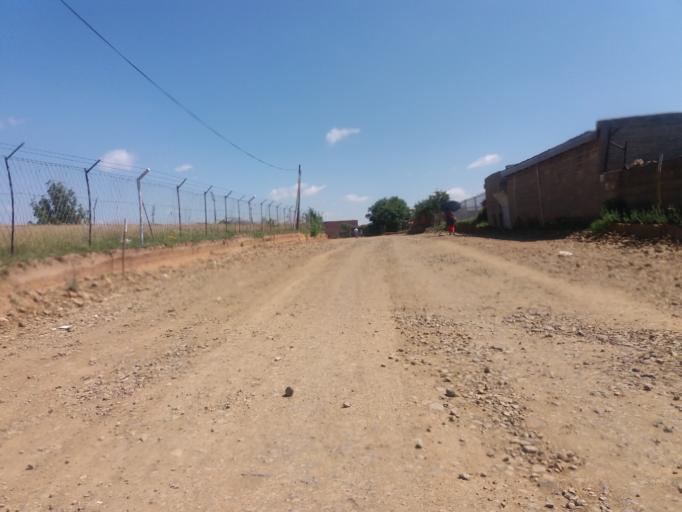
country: LS
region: Maseru
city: Maseru
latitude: -29.3168
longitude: 27.5039
